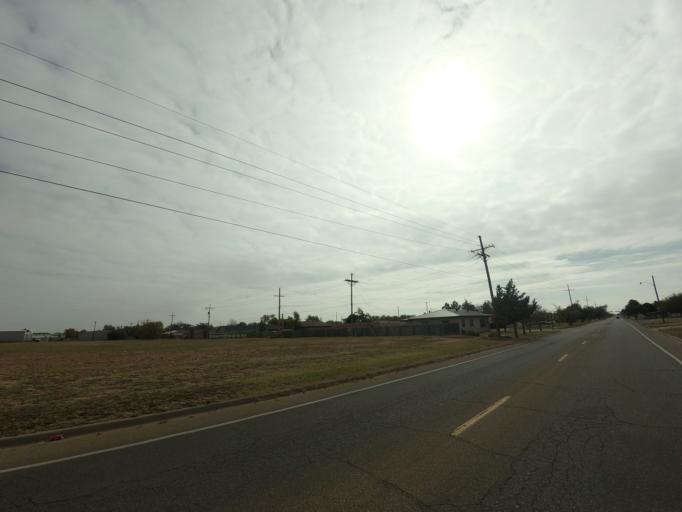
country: US
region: New Mexico
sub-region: Curry County
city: Clovis
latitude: 34.4307
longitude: -103.2141
